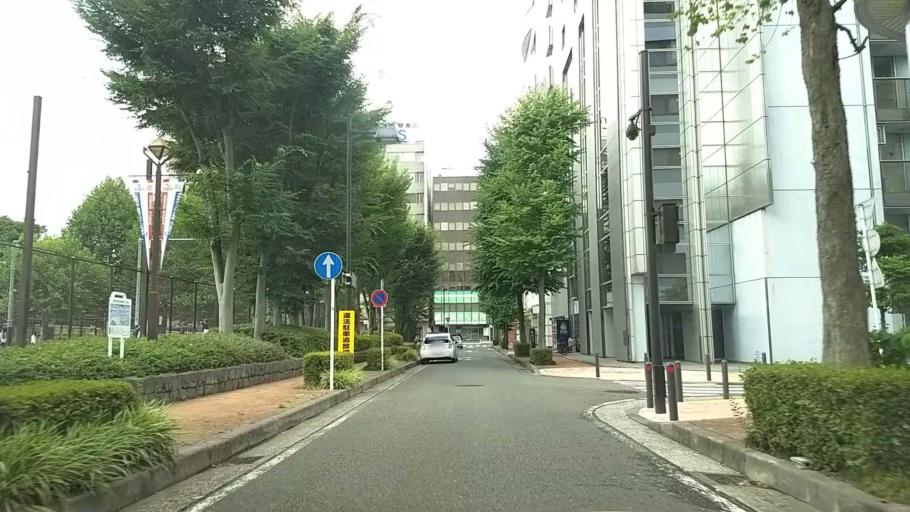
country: JP
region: Kanagawa
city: Yokohama
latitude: 35.5093
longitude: 139.6127
